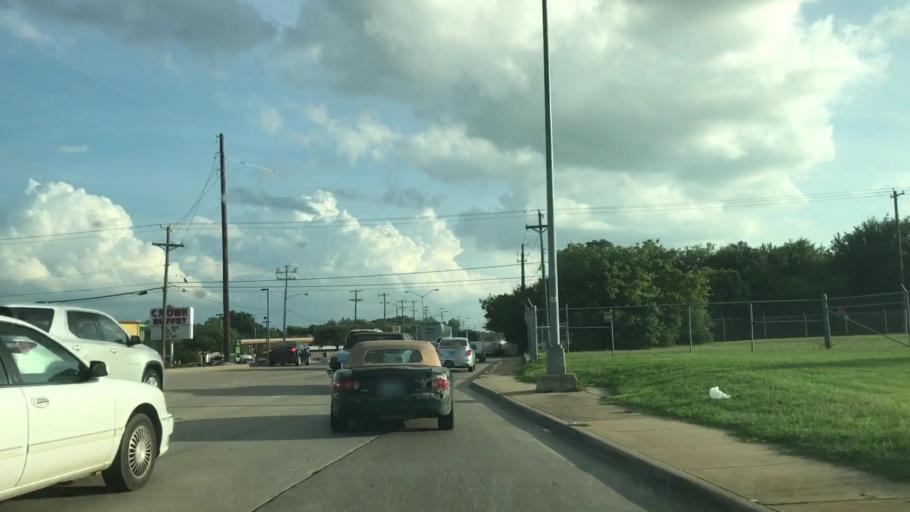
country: US
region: Texas
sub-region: Dallas County
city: Cockrell Hill
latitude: 32.7648
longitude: -96.8568
